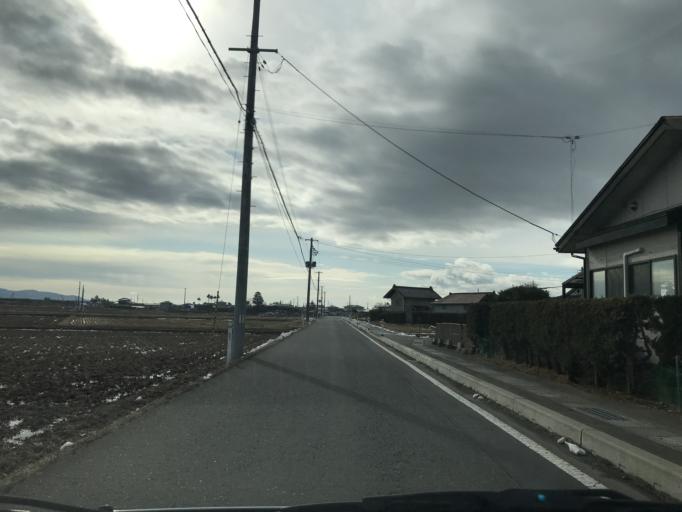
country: JP
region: Iwate
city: Mizusawa
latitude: 39.1748
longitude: 141.1311
